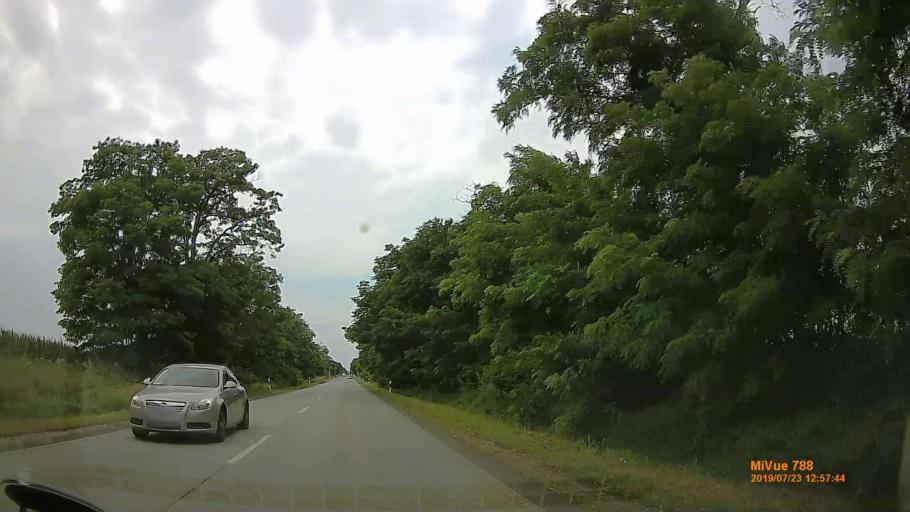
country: HU
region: Szabolcs-Szatmar-Bereg
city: Nagycserkesz
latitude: 47.9583
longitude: 21.4716
